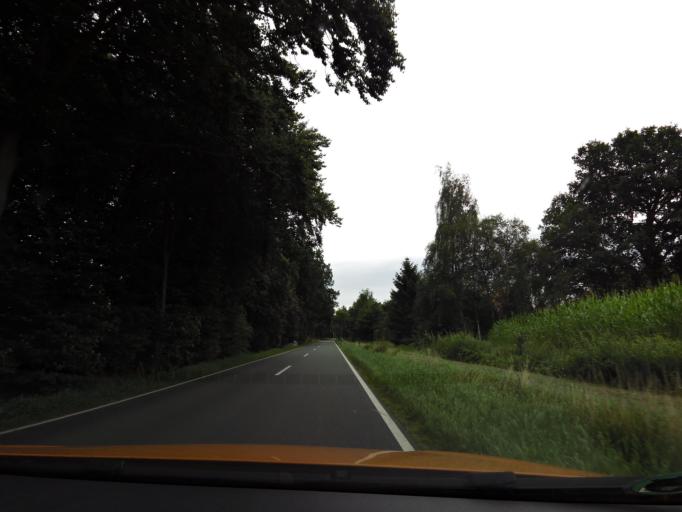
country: DE
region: Lower Saxony
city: Wiefelstede
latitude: 53.1933
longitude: 8.1404
